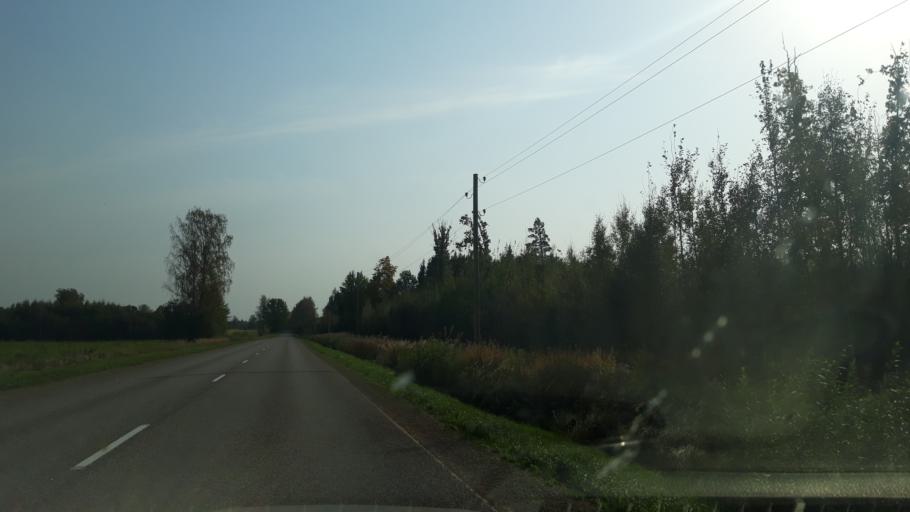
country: LV
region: Koceni
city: Koceni
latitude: 57.6229
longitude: 25.2736
